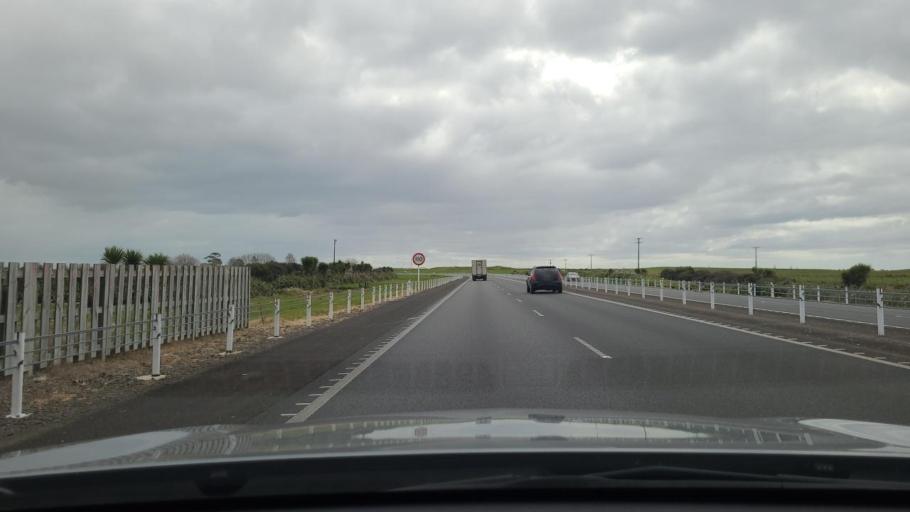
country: NZ
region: Bay of Plenty
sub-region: Western Bay of Plenty District
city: Maketu
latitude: -37.7405
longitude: 176.3522
